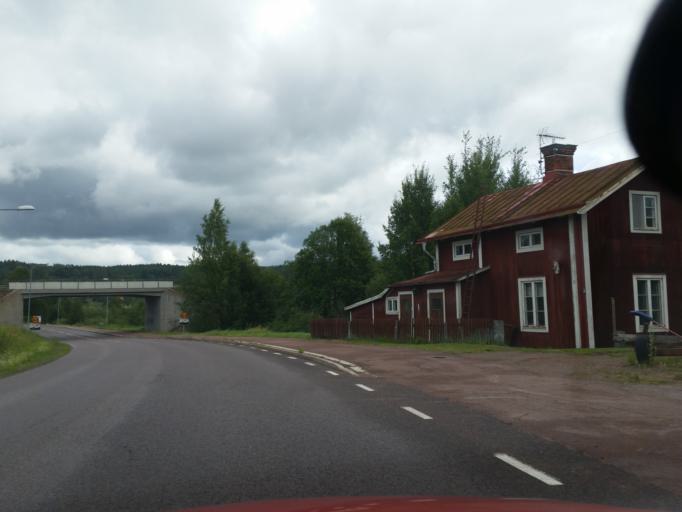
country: SE
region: Dalarna
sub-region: Leksand Municipality
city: Leksand
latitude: 60.7299
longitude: 15.0072
